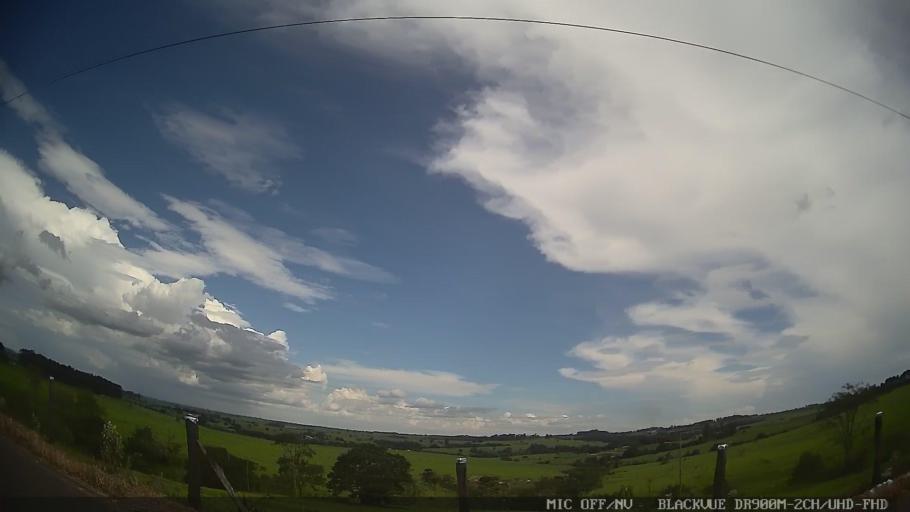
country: BR
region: Sao Paulo
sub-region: Conchas
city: Conchas
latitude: -22.9502
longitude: -47.9825
